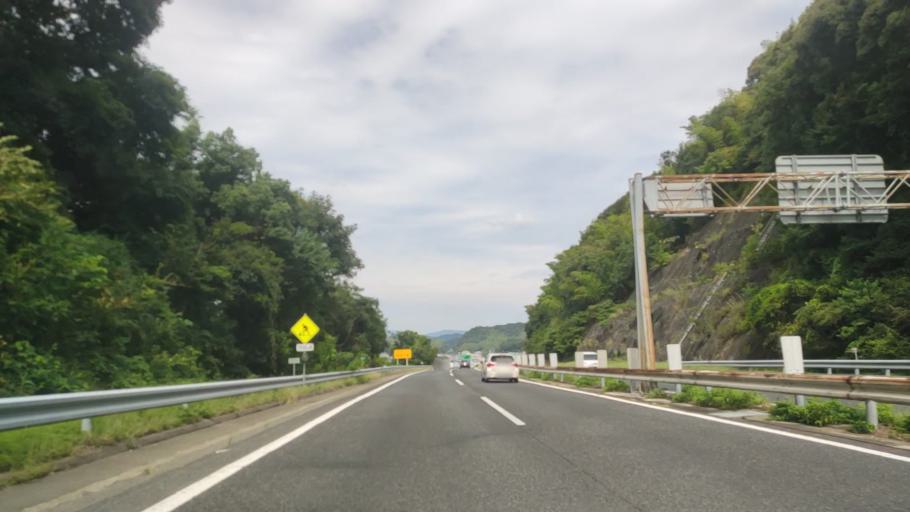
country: JP
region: Wakayama
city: Kainan
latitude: 34.1640
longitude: 135.2329
